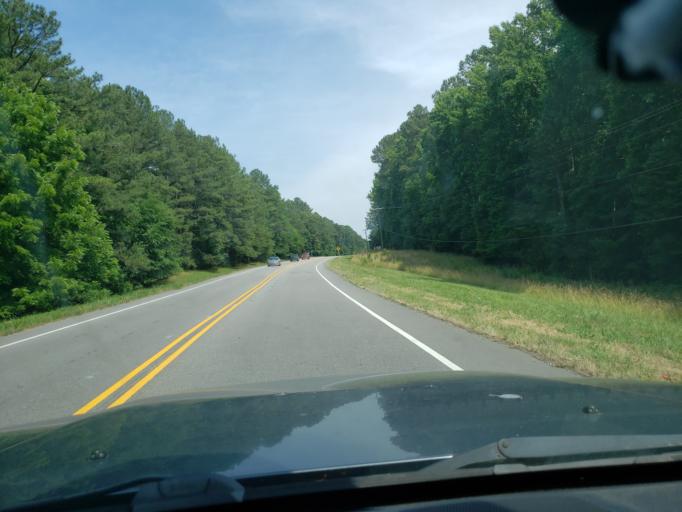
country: US
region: North Carolina
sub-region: Alamance County
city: Saxapahaw
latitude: 35.9311
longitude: -79.2055
